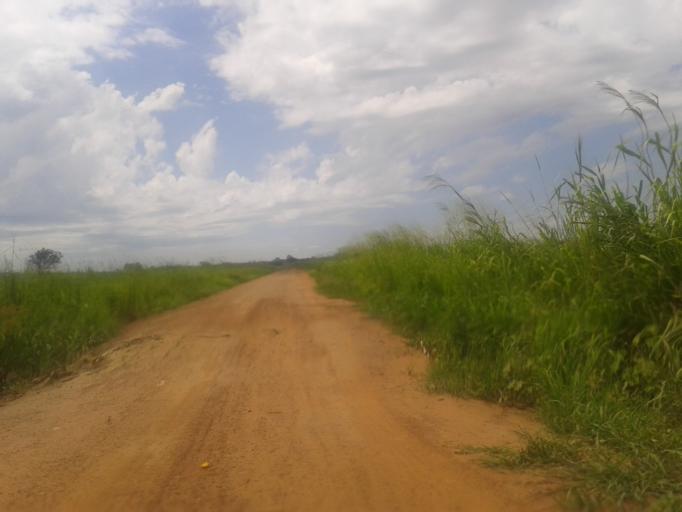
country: UG
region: Northern Region
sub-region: Gulu District
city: Gulu
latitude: 2.8228
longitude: 32.2647
